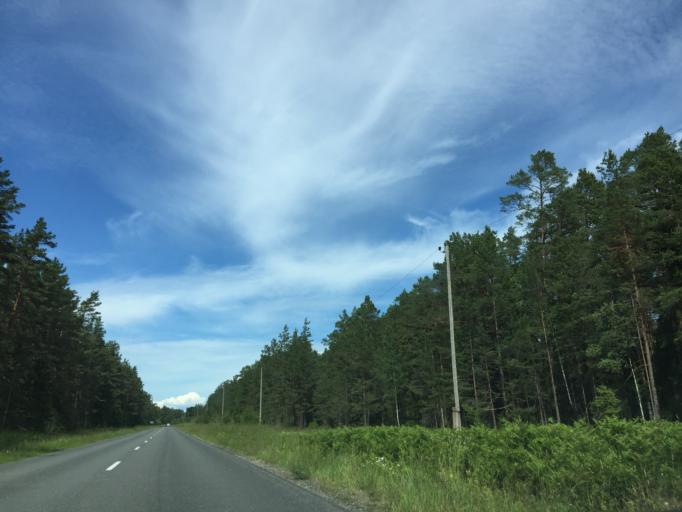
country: LV
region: Dundaga
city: Dundaga
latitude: 57.6617
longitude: 22.5703
